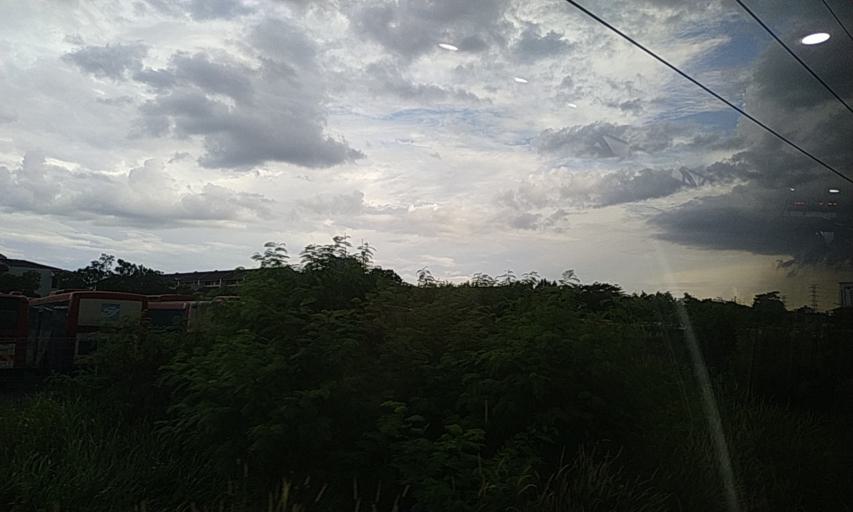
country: MY
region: Kuala Lumpur
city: Kuala Lumpur
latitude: 3.2187
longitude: 101.6724
